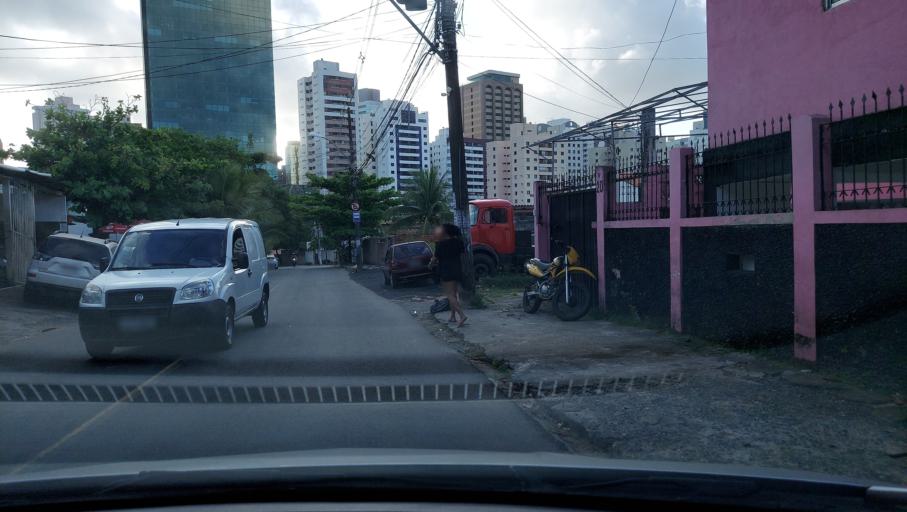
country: BR
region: Bahia
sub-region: Salvador
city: Salvador
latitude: -12.9866
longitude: -38.4466
